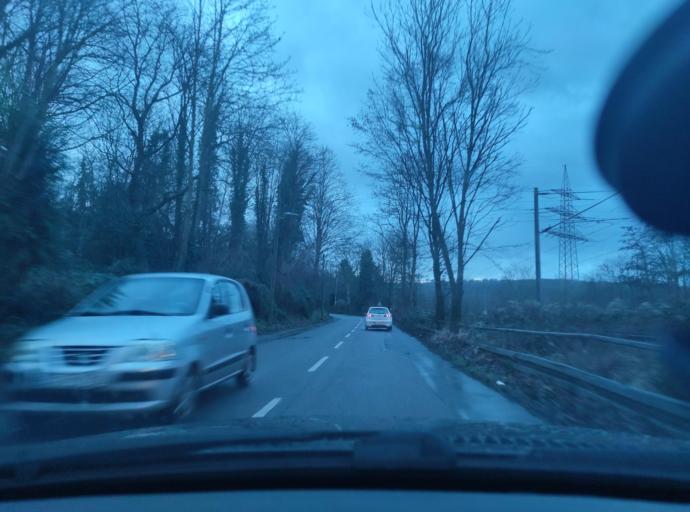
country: DE
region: North Rhine-Westphalia
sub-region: Regierungsbezirk Dusseldorf
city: Essen
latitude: 51.4278
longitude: 7.0687
